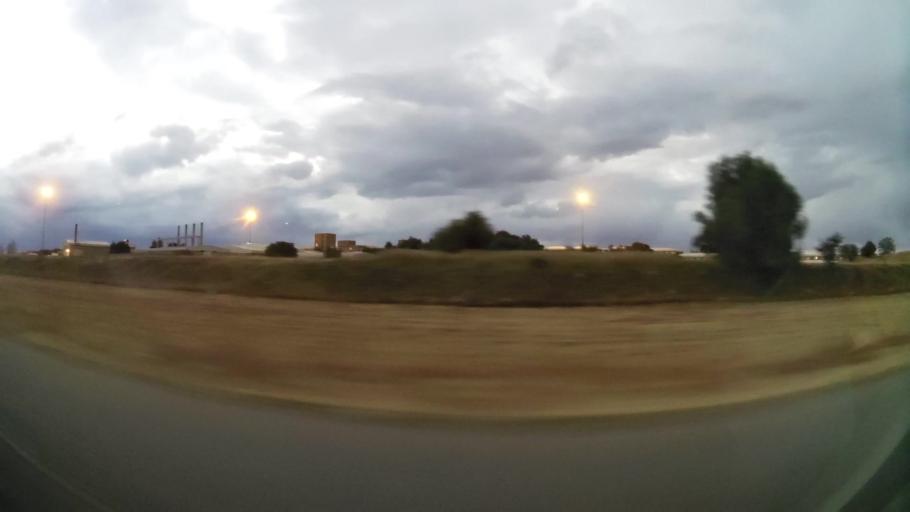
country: ZA
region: Orange Free State
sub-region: Lejweleputswa District Municipality
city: Welkom
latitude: -27.9529
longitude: 26.7896
